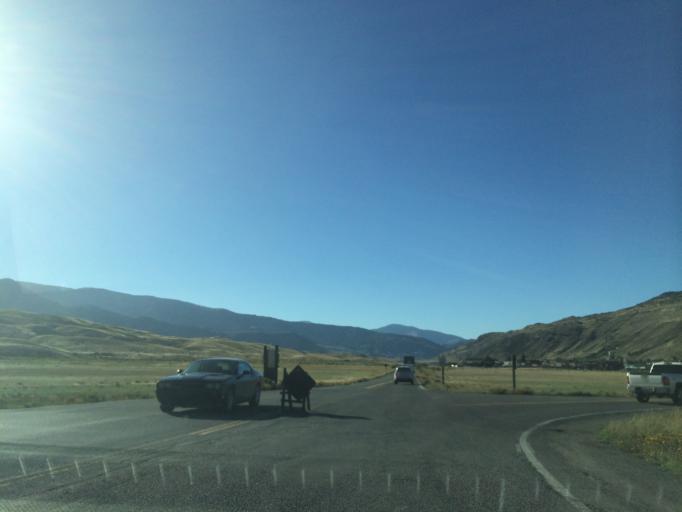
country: US
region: Montana
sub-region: Gallatin County
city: West Yellowstone
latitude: 45.0255
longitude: -110.7011
